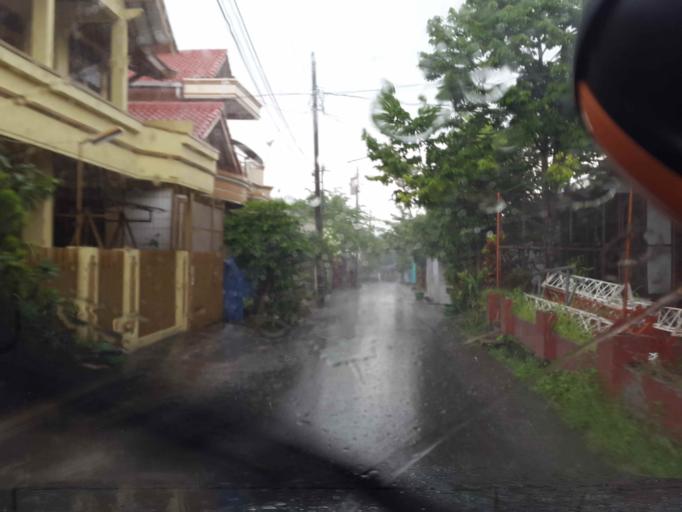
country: ID
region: Central Java
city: Salatiga
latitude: -7.3061
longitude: 110.4848
